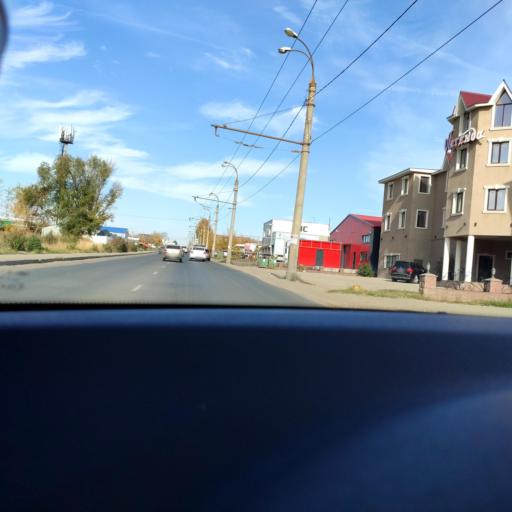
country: RU
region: Samara
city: Petra-Dubrava
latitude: 53.2540
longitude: 50.2666
